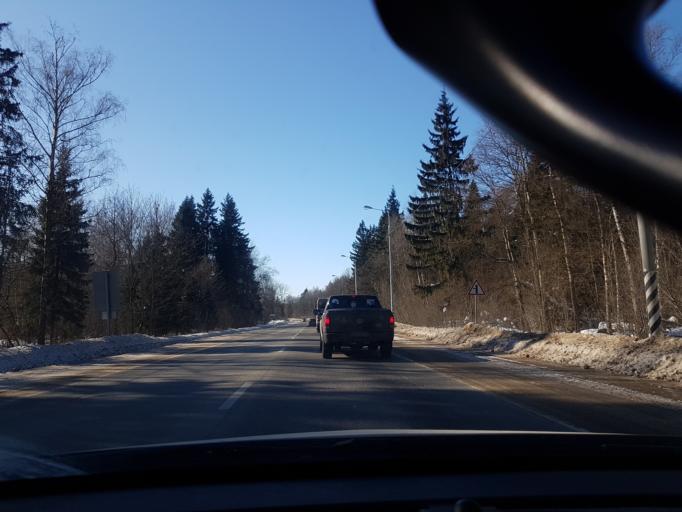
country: RU
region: Moskovskaya
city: Kostrovo
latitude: 55.9137
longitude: 36.7417
